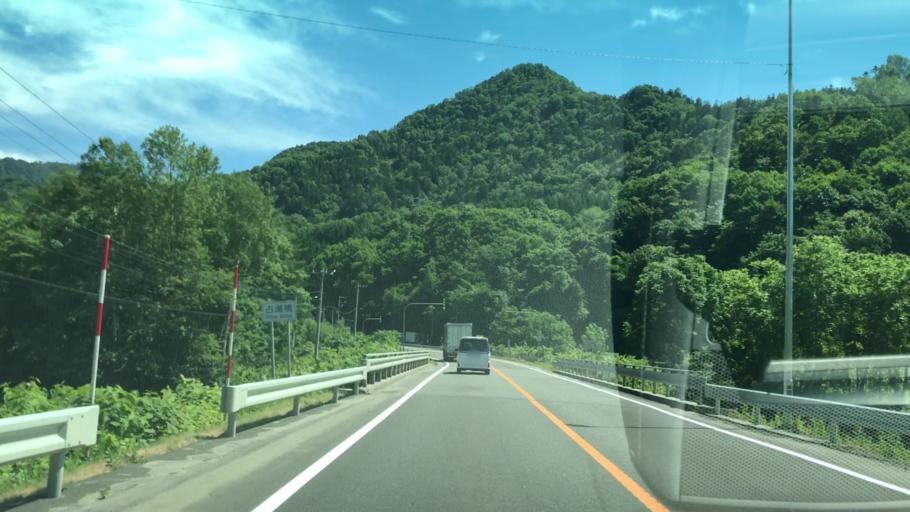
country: JP
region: Hokkaido
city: Shimo-furano
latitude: 42.9061
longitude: 142.5776
